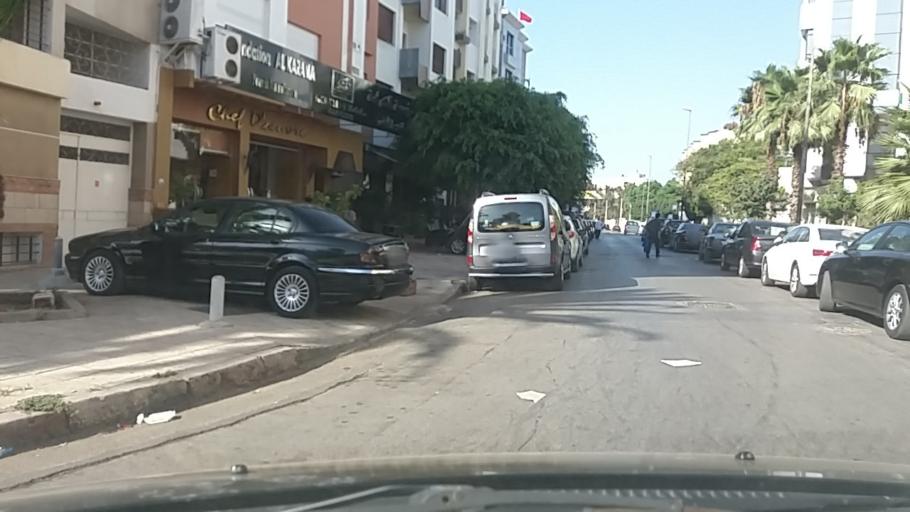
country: MA
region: Rabat-Sale-Zemmour-Zaer
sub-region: Rabat
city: Rabat
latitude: 34.0153
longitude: -6.8287
